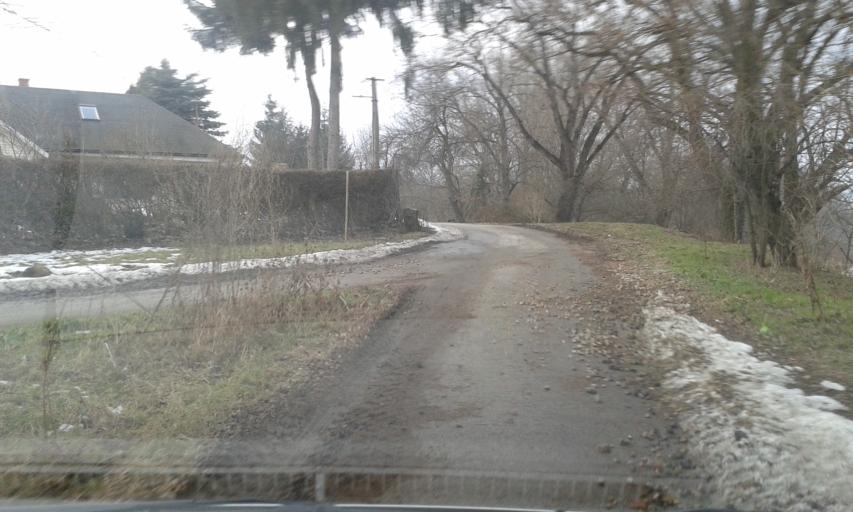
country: SK
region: Nitriansky
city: Levice
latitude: 48.1976
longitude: 18.5263
